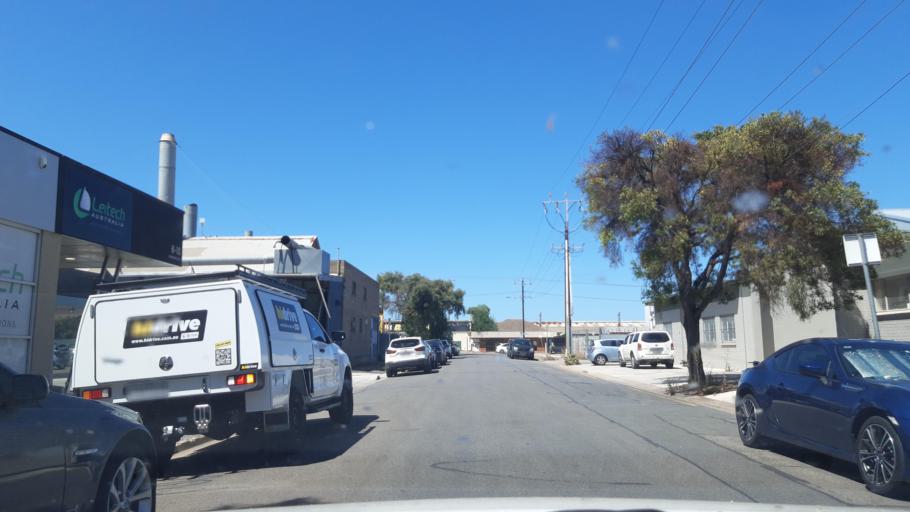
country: AU
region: South Australia
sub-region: Marion
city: Clovelly Park
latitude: -34.9901
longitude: 138.5736
